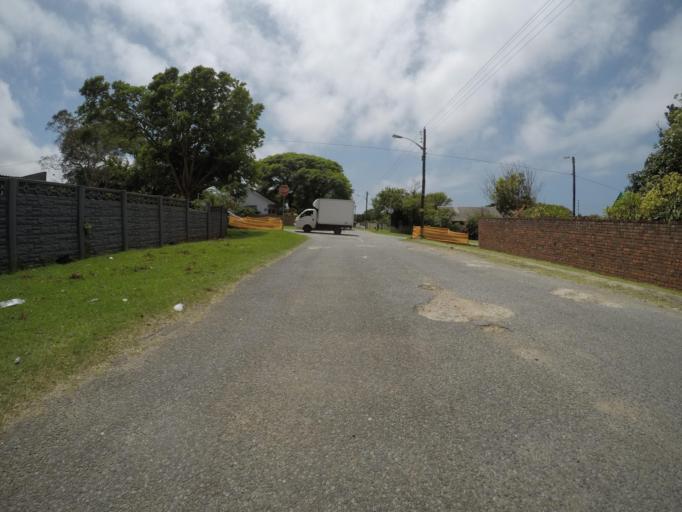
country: ZA
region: Eastern Cape
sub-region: Buffalo City Metropolitan Municipality
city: East London
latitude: -32.9379
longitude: 28.0051
